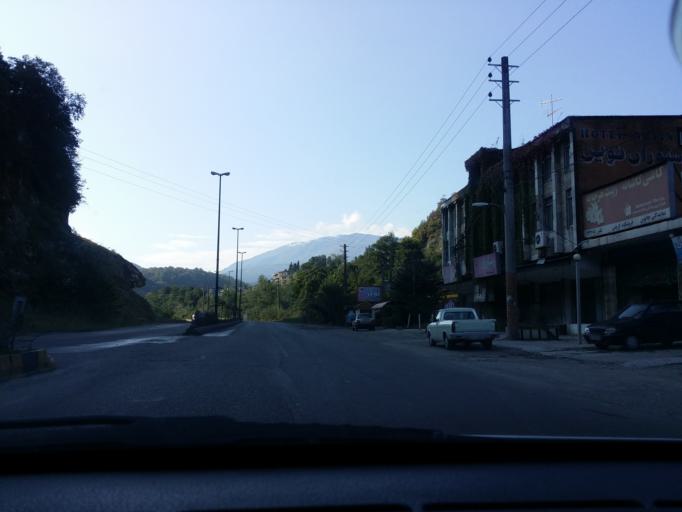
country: IR
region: Mazandaran
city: Chalus
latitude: 36.6400
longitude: 51.4111
